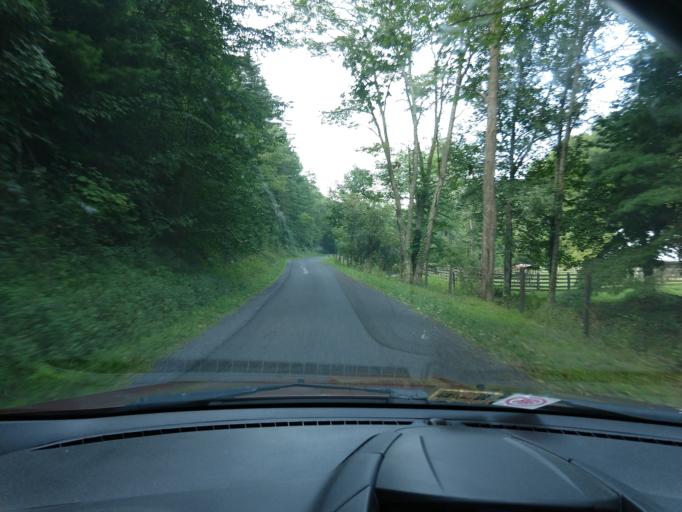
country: US
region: Virginia
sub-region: City of Covington
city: Covington
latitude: 37.9040
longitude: -80.0815
